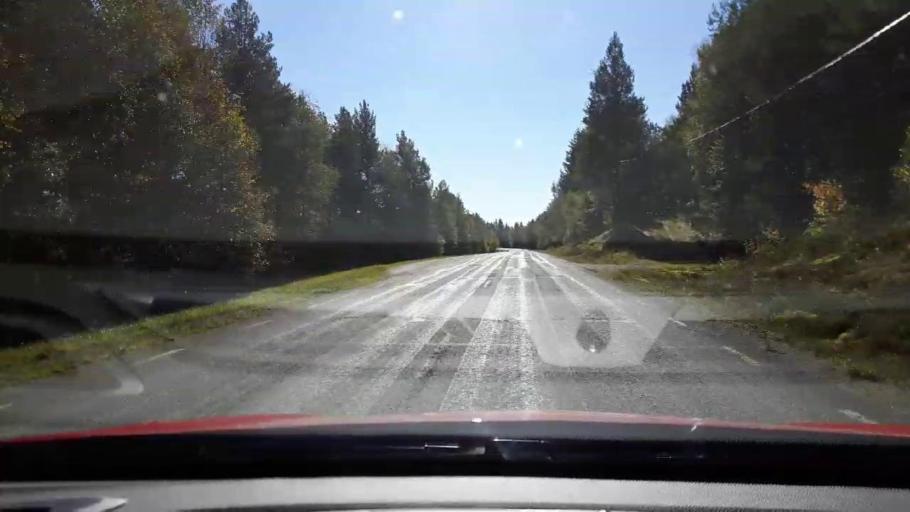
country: SE
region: Jaemtland
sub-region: Harjedalens Kommun
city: Sveg
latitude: 62.3428
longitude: 14.0374
